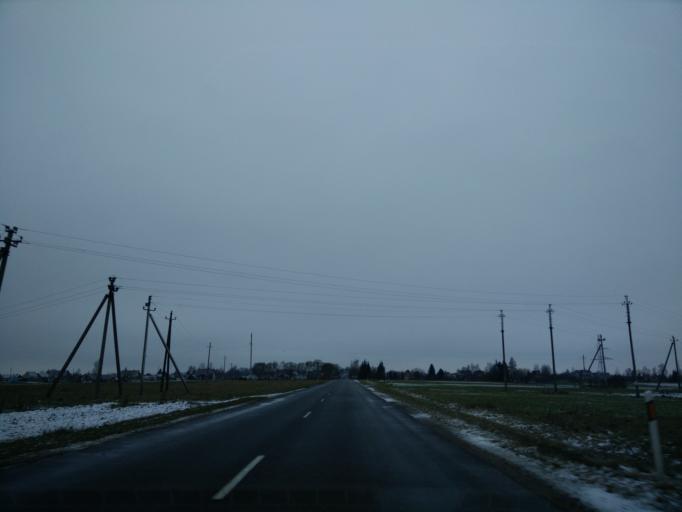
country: LT
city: Ariogala
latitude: 55.3553
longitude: 23.3773
